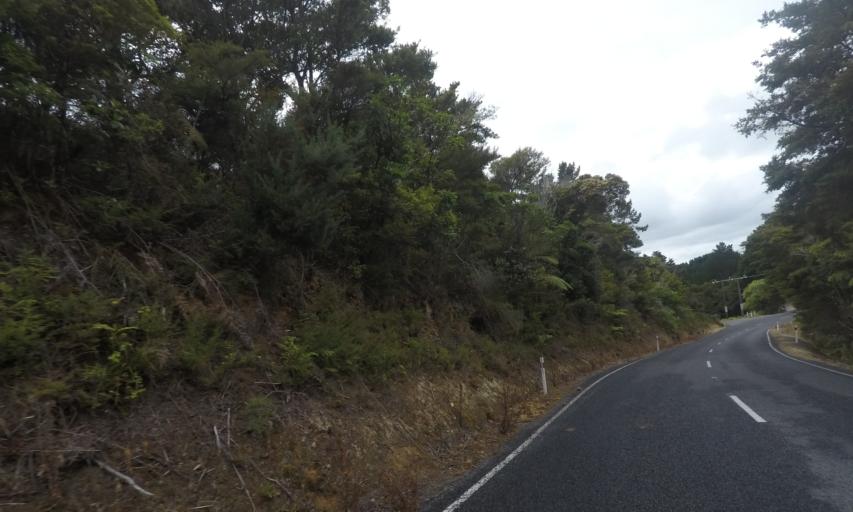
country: NZ
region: Northland
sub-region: Whangarei
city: Whangarei
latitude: -35.7584
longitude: 174.4545
